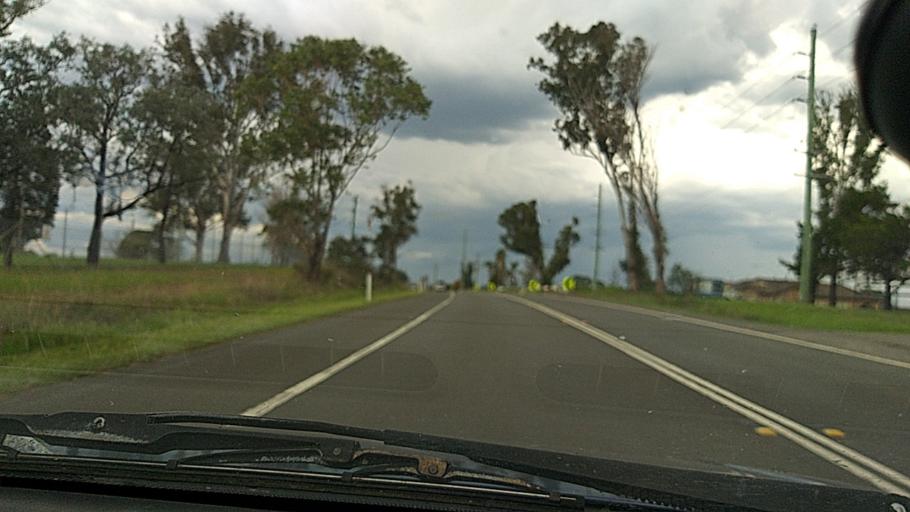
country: AU
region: New South Wales
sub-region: Penrith Municipality
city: Glenmore Park
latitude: -33.8156
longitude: 150.6892
